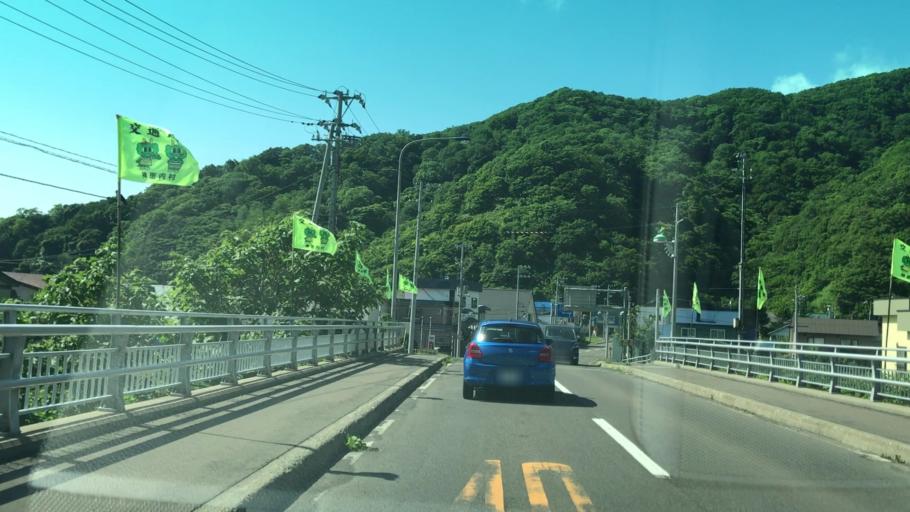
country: JP
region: Hokkaido
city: Iwanai
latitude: 43.1422
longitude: 140.4339
